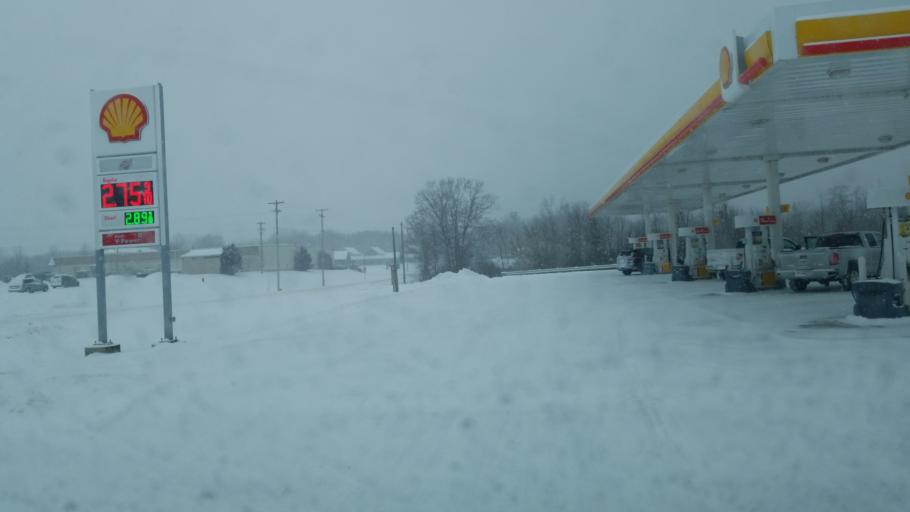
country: US
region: Michigan
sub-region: Mecosta County
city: Canadian Lakes
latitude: 43.5888
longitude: -85.2844
